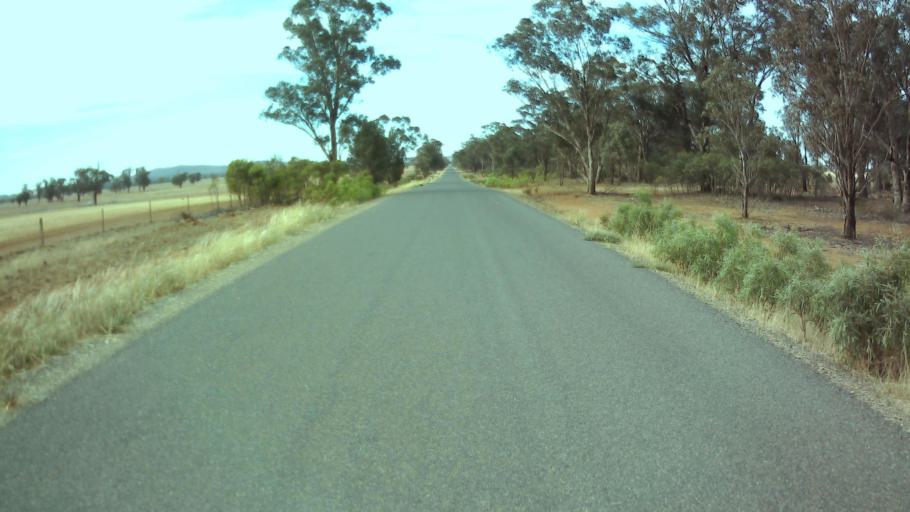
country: AU
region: New South Wales
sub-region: Weddin
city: Grenfell
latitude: -33.8850
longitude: 147.8553
